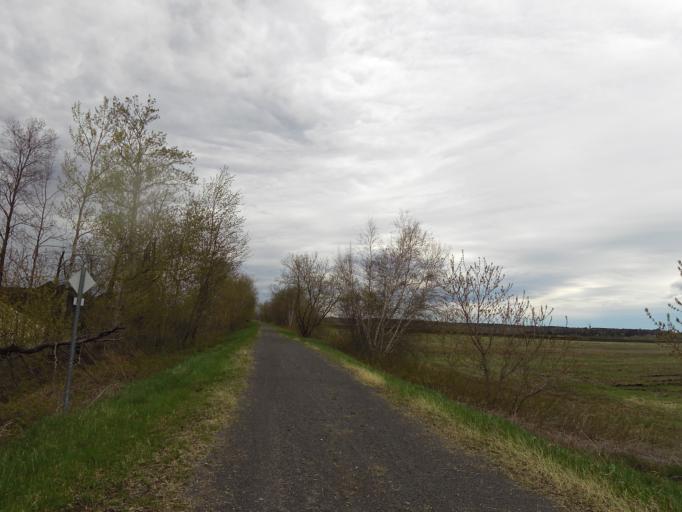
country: CA
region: Quebec
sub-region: Outaouais
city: Papineauville
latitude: 45.5403
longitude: -74.8579
